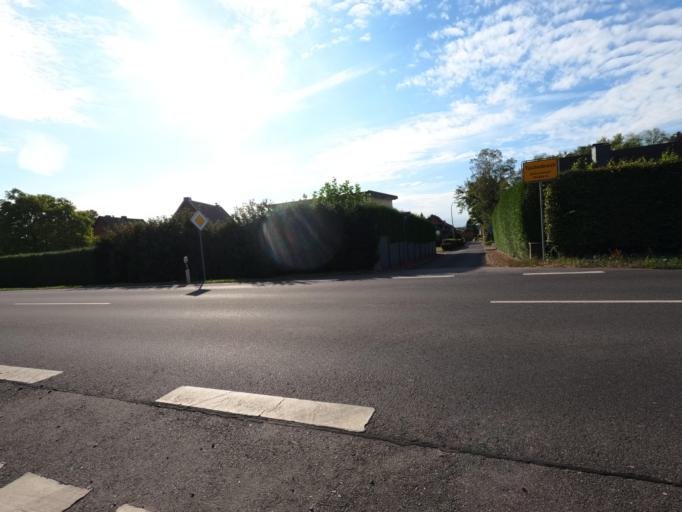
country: DE
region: North Rhine-Westphalia
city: Wegberg
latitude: 51.1202
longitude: 6.2519
